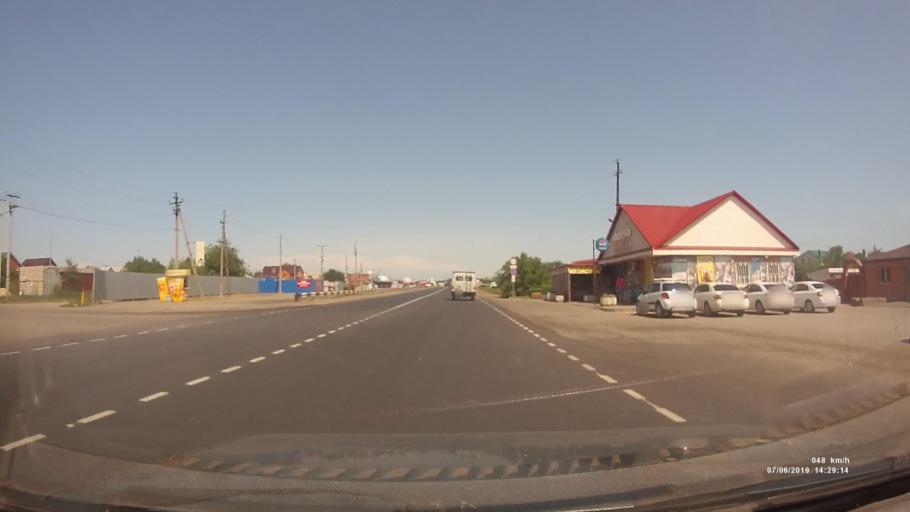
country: RU
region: Rostov
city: Kuleshovka
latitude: 47.0804
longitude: 39.5757
